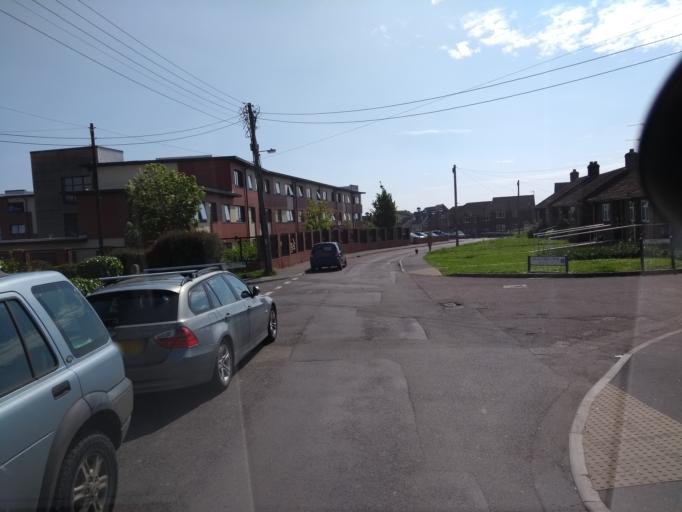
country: GB
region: England
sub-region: Somerset
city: Chard
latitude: 50.8702
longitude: -2.9609
